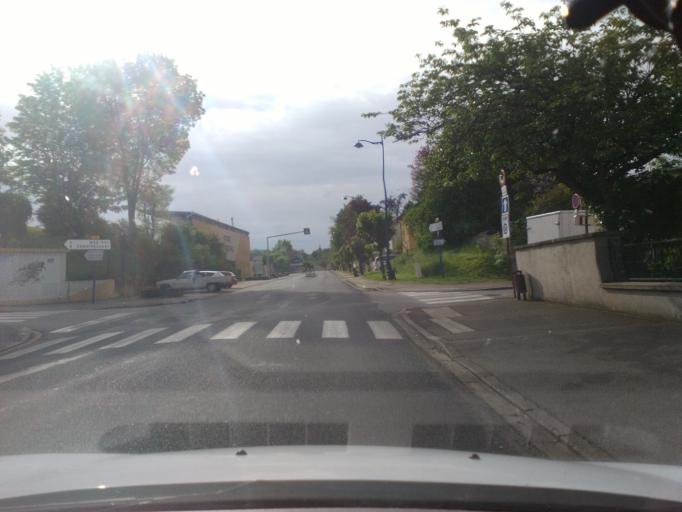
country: FR
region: Lorraine
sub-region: Departement des Vosges
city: Mirecourt
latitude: 48.3025
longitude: 6.1395
